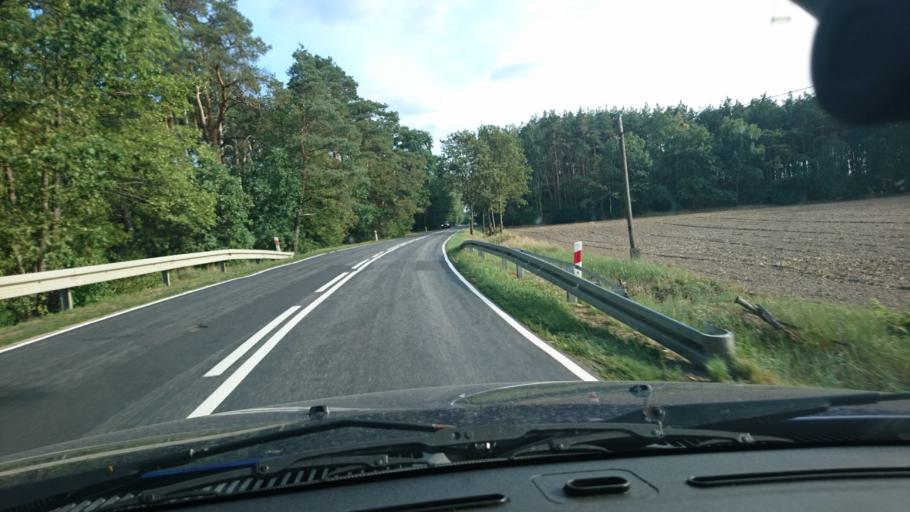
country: PL
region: Greater Poland Voivodeship
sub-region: Powiat krotoszynski
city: Sulmierzyce
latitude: 51.6219
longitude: 17.5000
